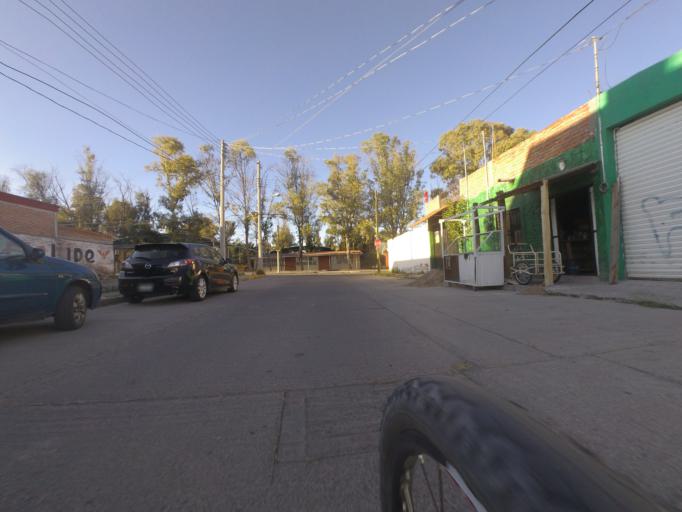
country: MX
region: Aguascalientes
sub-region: Aguascalientes
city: La Loma de los Negritos
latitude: 21.8515
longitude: -102.3407
